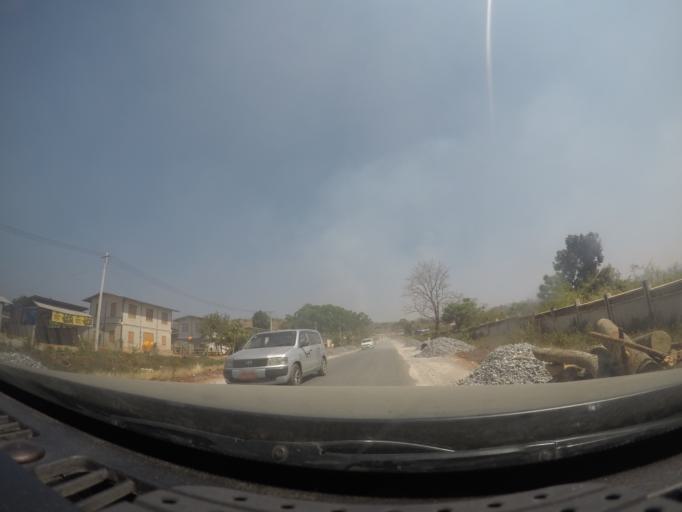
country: MM
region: Shan
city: Taunggyi
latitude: 20.8169
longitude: 97.2111
